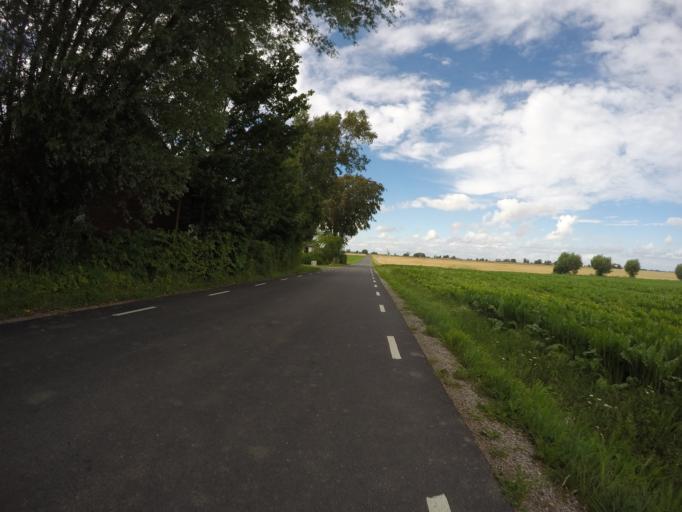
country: SE
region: Skane
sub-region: Ystads Kommun
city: Kopingebro
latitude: 55.4180
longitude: 14.1491
